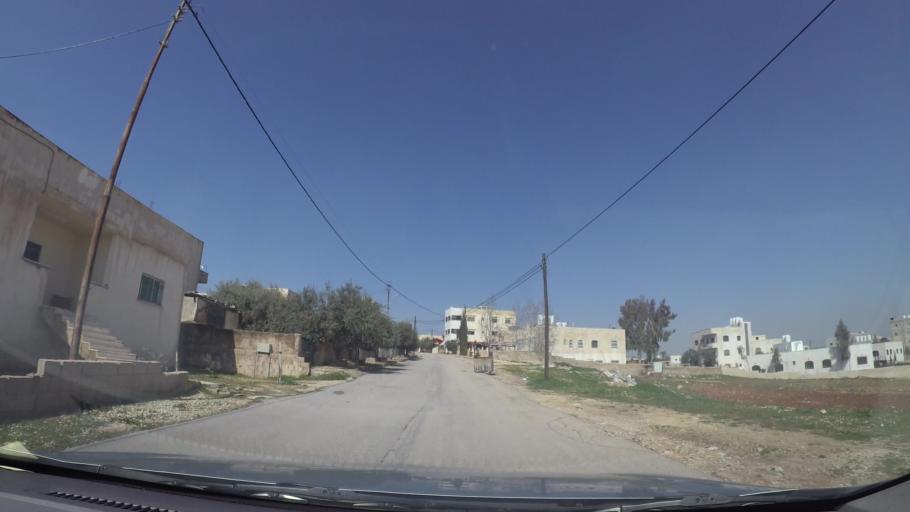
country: JO
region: Amman
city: Al Bunayyat ash Shamaliyah
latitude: 31.8941
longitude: 35.8948
